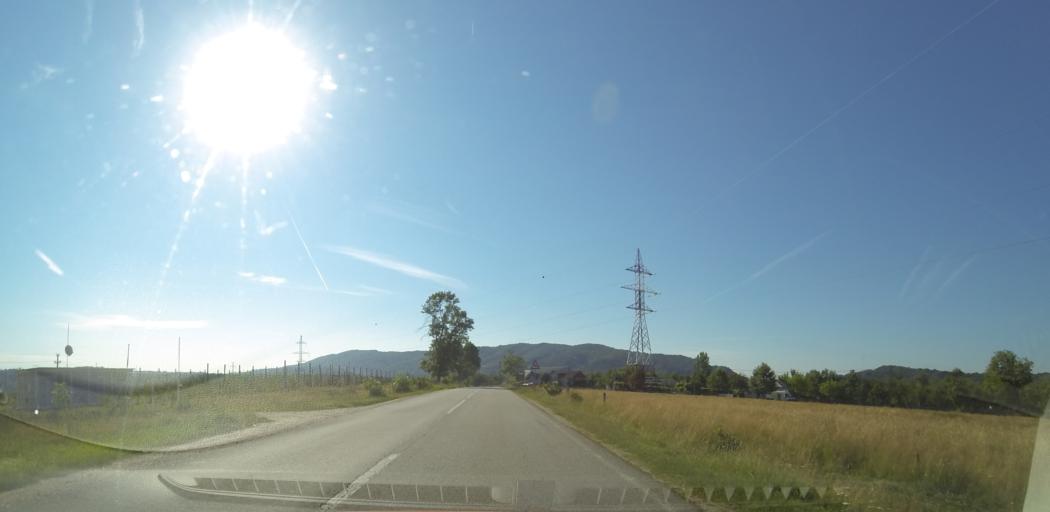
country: RO
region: Valcea
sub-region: Comuna Slatioara
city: Slatioara
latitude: 45.1251
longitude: 23.8773
